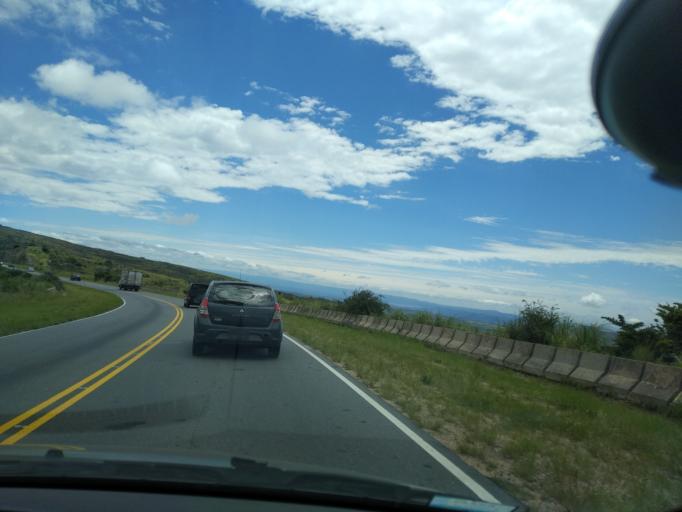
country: AR
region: Cordoba
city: Cuesta Blanca
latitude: -31.6370
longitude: -64.6765
